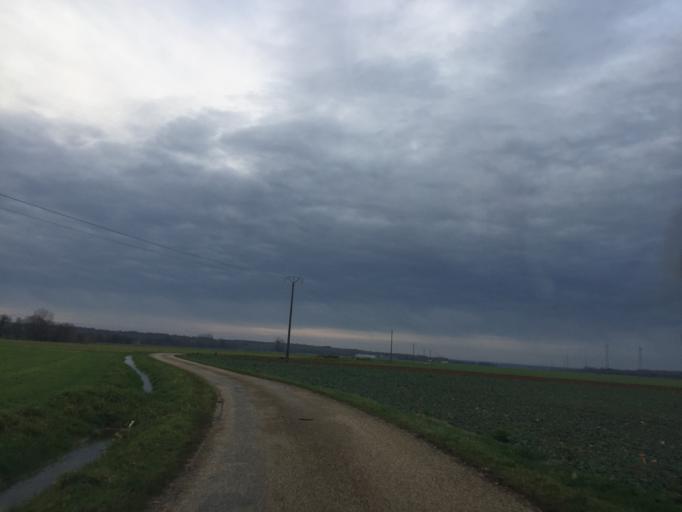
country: FR
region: Franche-Comte
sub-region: Departement du Jura
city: Mont-sous-Vaudrey
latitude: 46.9401
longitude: 5.6747
